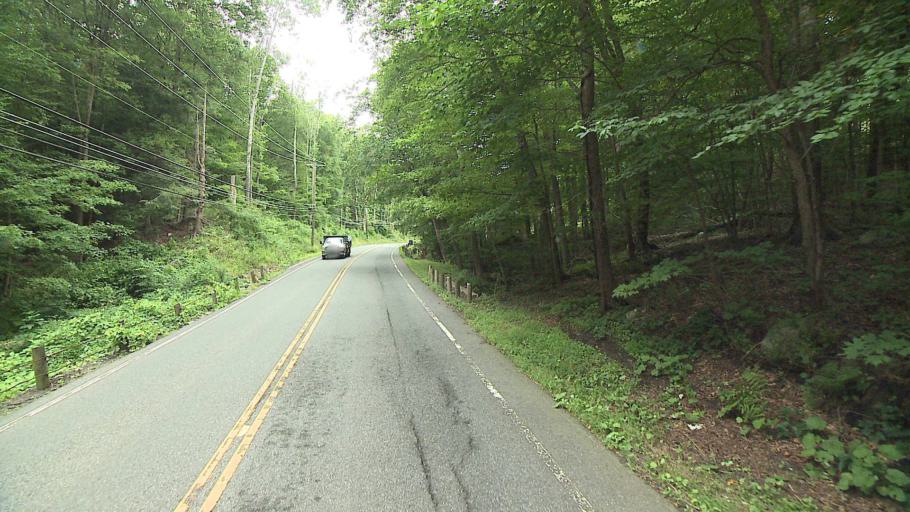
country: US
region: Connecticut
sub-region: Litchfield County
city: New Preston
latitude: 41.6234
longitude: -73.2990
